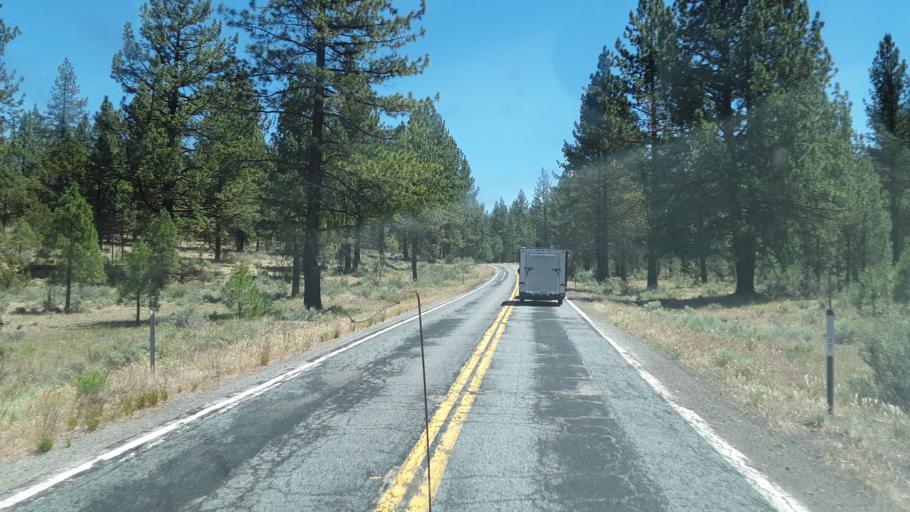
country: US
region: California
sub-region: Modoc County
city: Alturas
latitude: 40.9820
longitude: -120.7926
